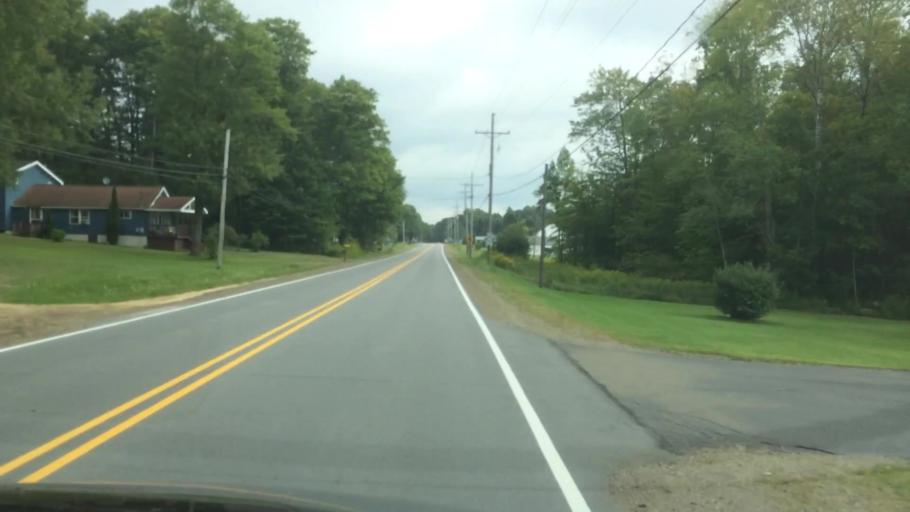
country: US
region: Pennsylvania
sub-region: McKean County
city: Bradford
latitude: 41.8756
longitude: -78.5820
